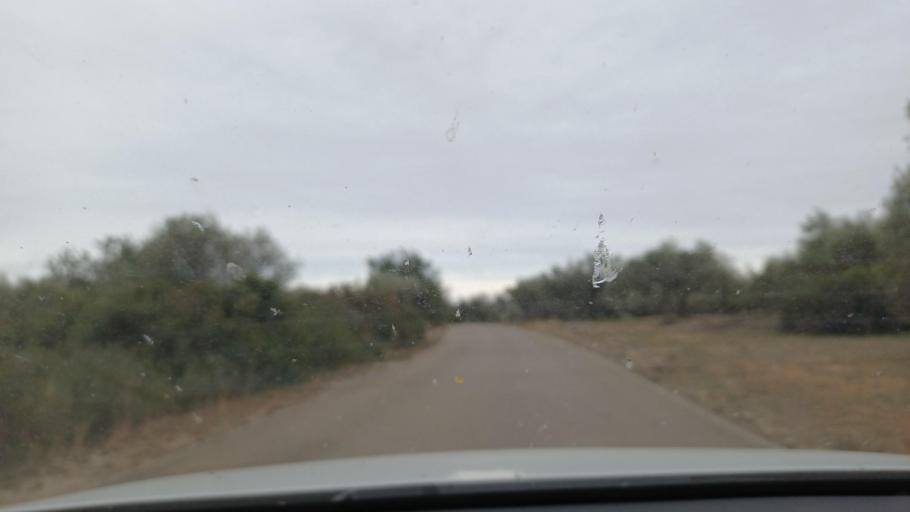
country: ES
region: Valencia
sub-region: Provincia de Castello
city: Canet lo Roig
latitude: 40.5946
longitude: 0.2837
